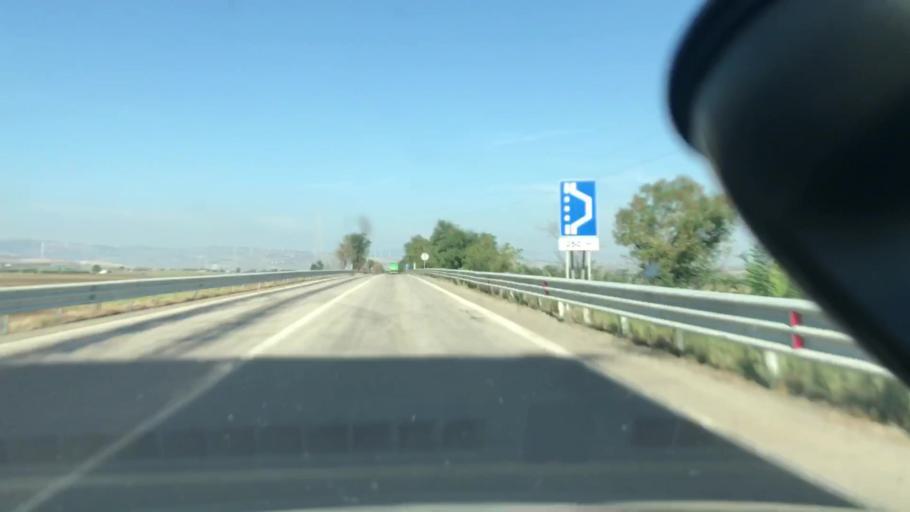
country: IT
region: Basilicate
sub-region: Provincia di Potenza
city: Zona 179
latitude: 41.0756
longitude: 15.6421
